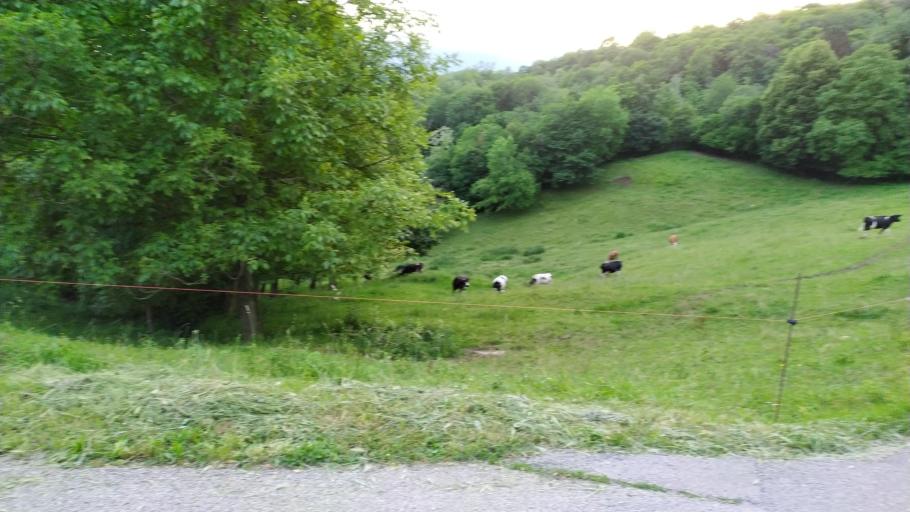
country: IT
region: Veneto
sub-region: Provincia di Vicenza
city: Valdagno
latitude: 45.6788
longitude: 11.3138
